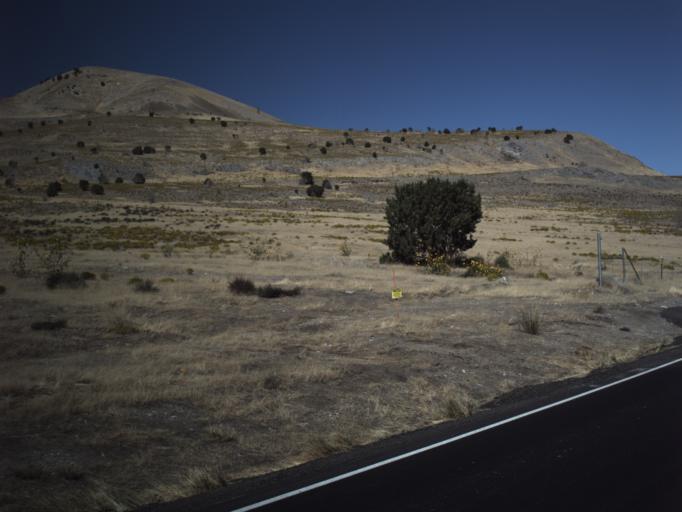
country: US
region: Utah
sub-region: Utah County
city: Saratoga Springs
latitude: 40.2240
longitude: -111.8768
